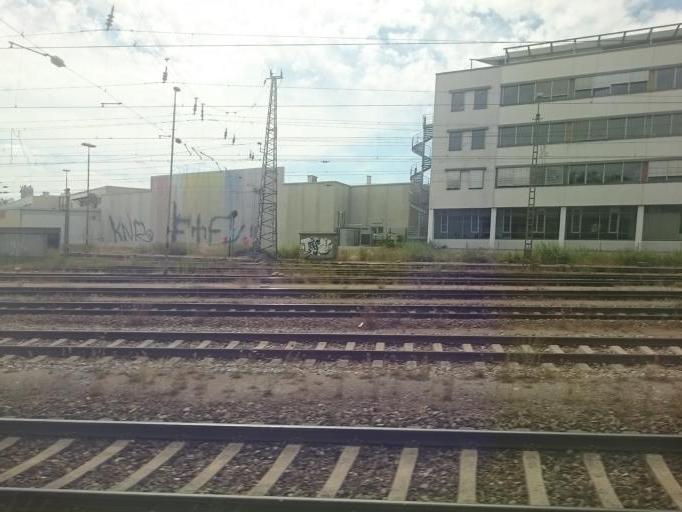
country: DE
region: Bavaria
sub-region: Upper Bavaria
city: Munich
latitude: 48.1236
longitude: 11.5506
